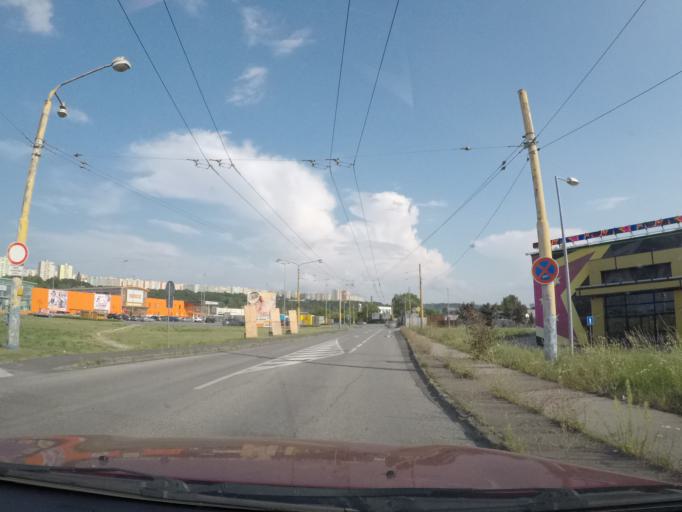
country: SK
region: Kosicky
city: Kosice
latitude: 48.7401
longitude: 21.2676
